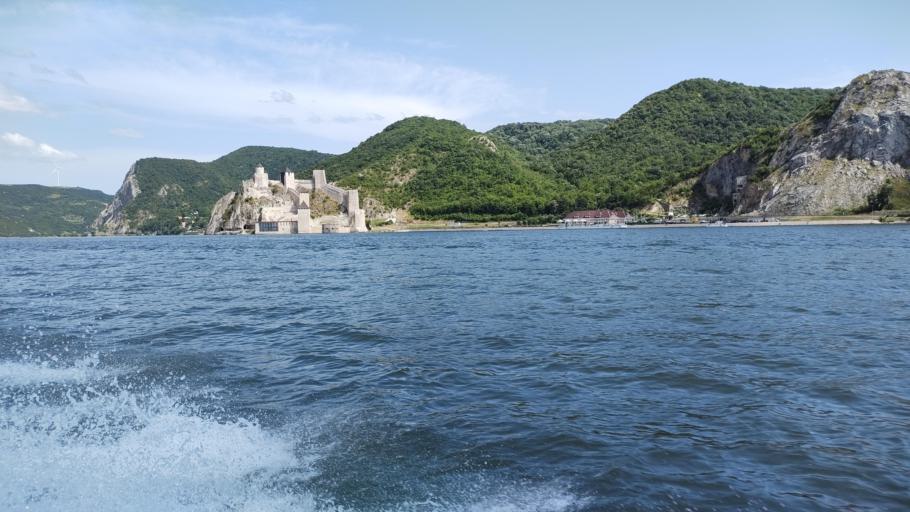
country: RO
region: Caras-Severin
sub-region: Comuna Pescari
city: Coronini
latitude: 44.6637
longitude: 21.6704
